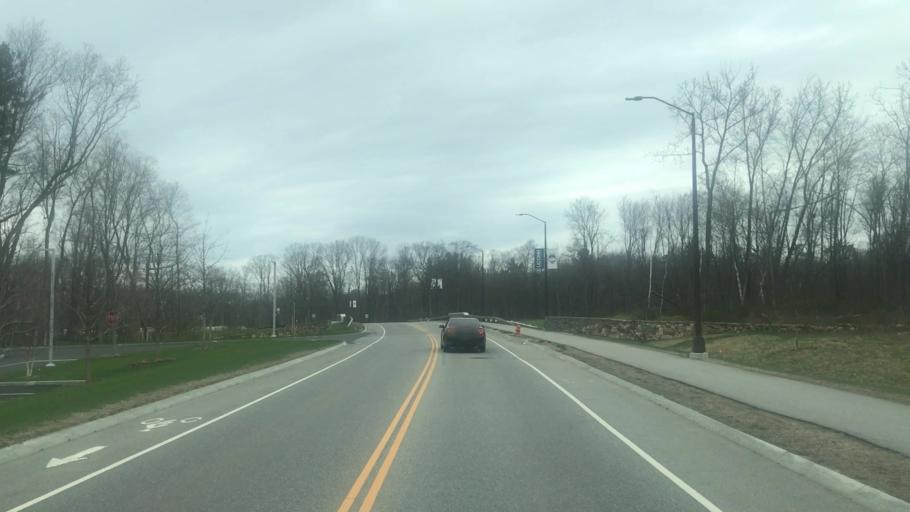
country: US
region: Connecticut
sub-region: Tolland County
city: Storrs
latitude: 41.8194
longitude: -72.2655
